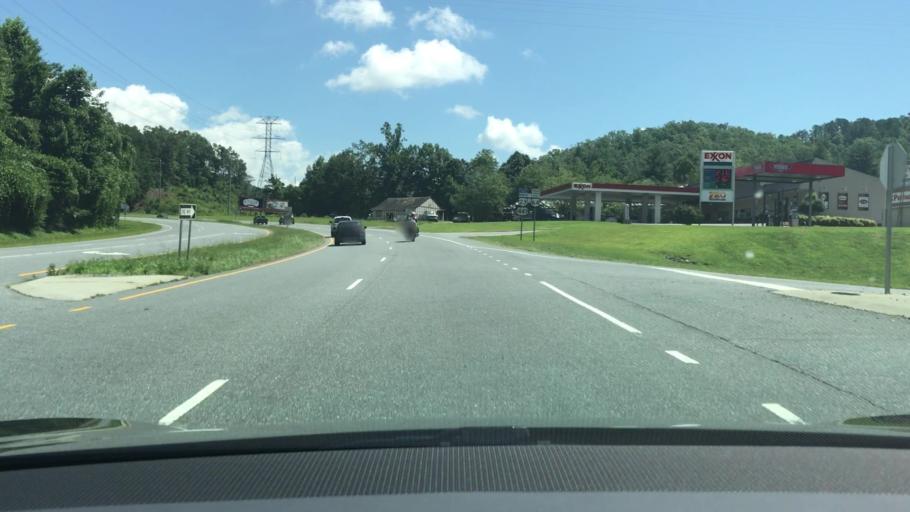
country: US
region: North Carolina
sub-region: Jackson County
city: Sylva
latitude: 35.3358
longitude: -83.2542
